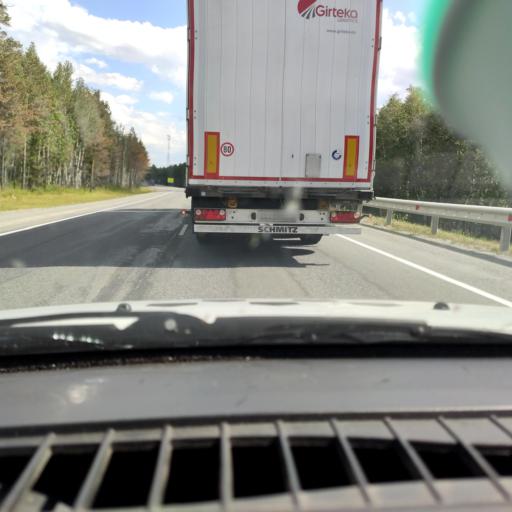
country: RU
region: Chelyabinsk
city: Zlatoust
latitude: 55.0236
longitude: 59.7256
